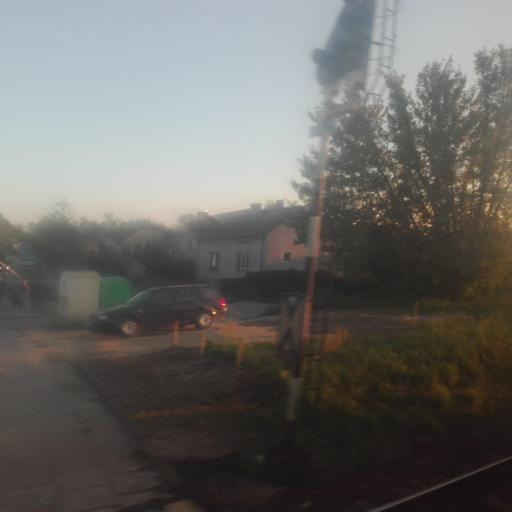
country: PL
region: Masovian Voivodeship
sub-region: Powiat warszawski zachodni
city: Bieniewice
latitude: 52.1898
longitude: 20.5267
